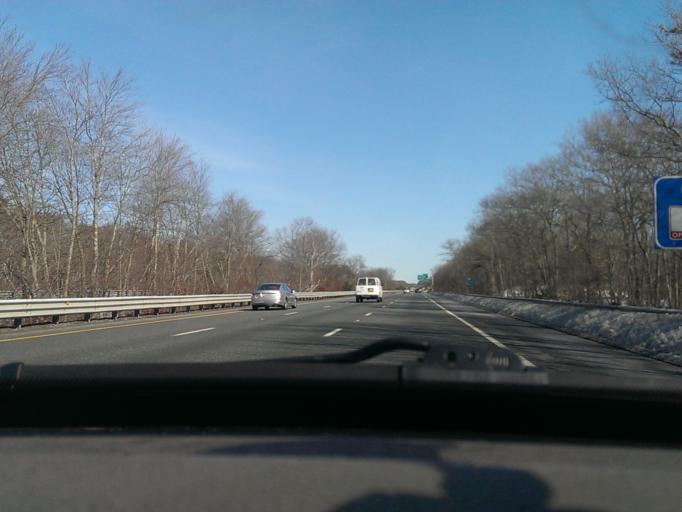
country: US
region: Massachusetts
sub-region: Bristol County
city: Head of Westport
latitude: 41.6576
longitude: -71.0467
